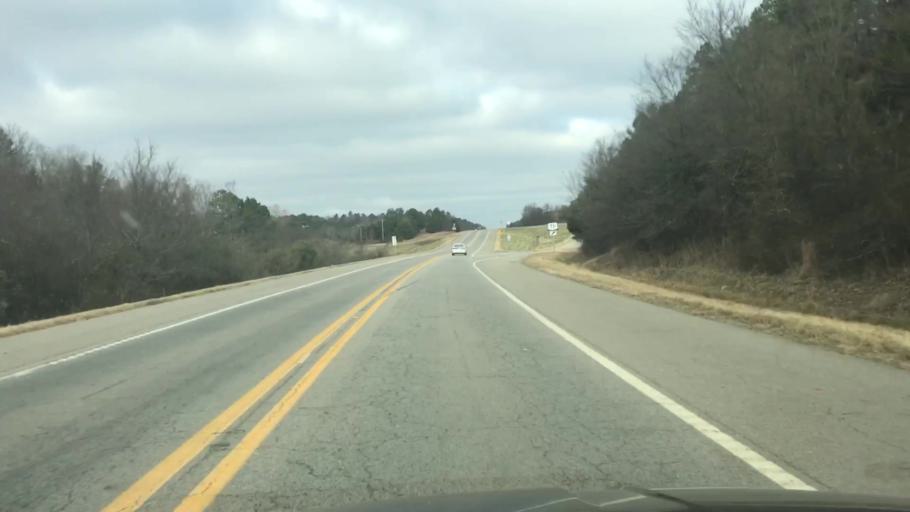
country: US
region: Arkansas
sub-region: Scott County
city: Waldron
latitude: 34.8535
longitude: -94.0648
